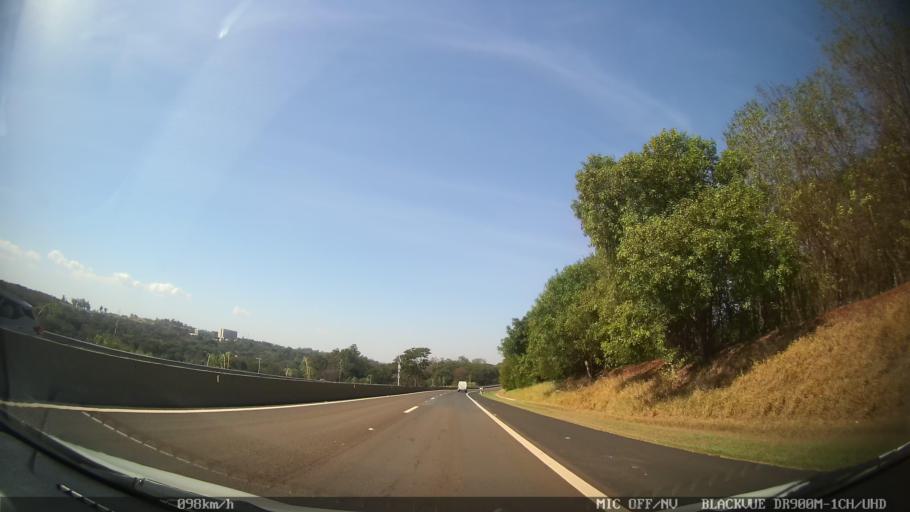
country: BR
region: Sao Paulo
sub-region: Ribeirao Preto
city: Ribeirao Preto
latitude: -21.1675
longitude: -47.8707
